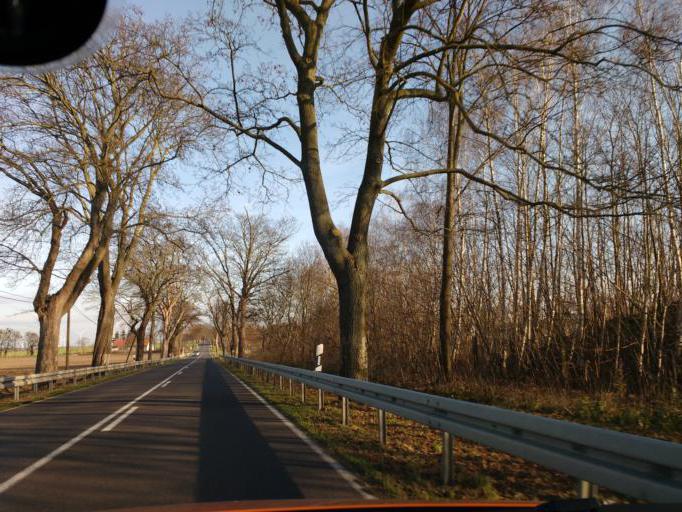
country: DE
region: Brandenburg
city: Protzel
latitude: 52.6553
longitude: 14.0300
